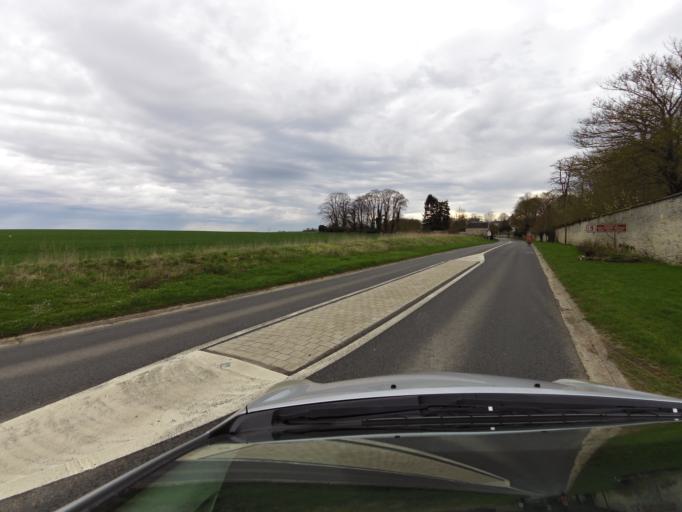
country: FR
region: Picardie
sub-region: Departement de l'Oise
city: Chamant
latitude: 49.1968
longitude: 2.6229
